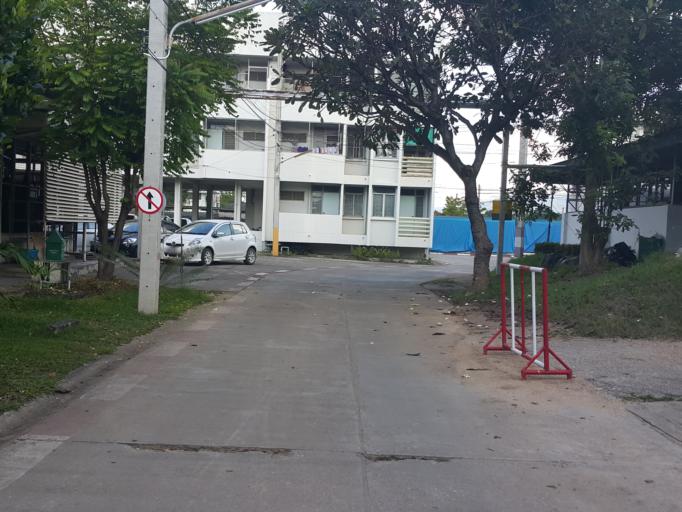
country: TH
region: Lampang
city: Lampang
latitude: 18.2875
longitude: 99.5073
